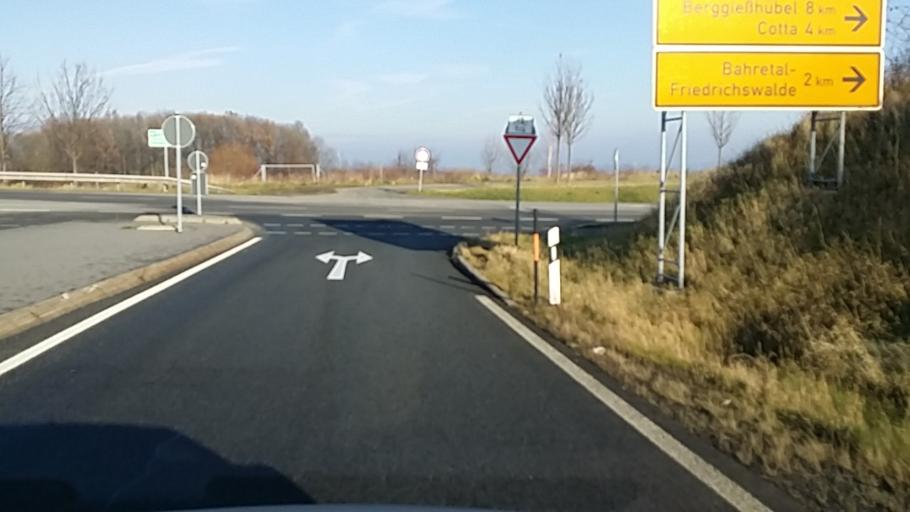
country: DE
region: Saxony
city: Dohma
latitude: 50.8984
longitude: 13.8899
